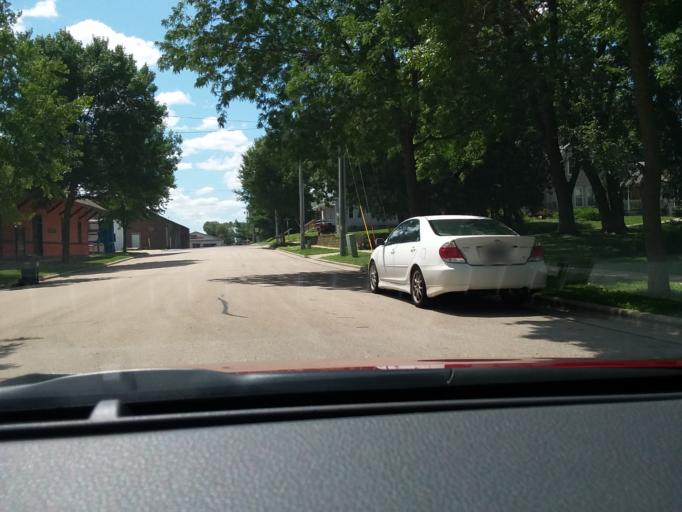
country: US
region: Wisconsin
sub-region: Dane County
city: De Forest
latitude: 43.2461
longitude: -89.3417
